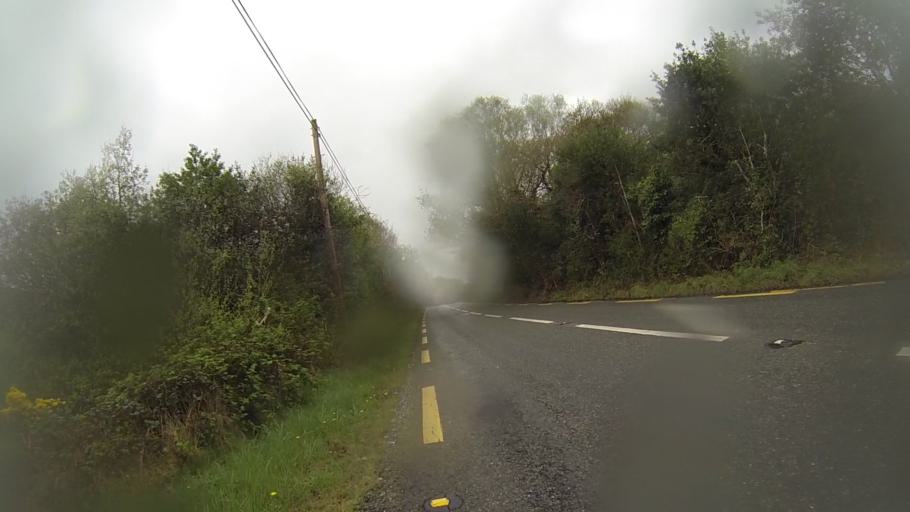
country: IE
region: Munster
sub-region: Ciarrai
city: Kenmare
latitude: 51.8185
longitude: -9.5317
